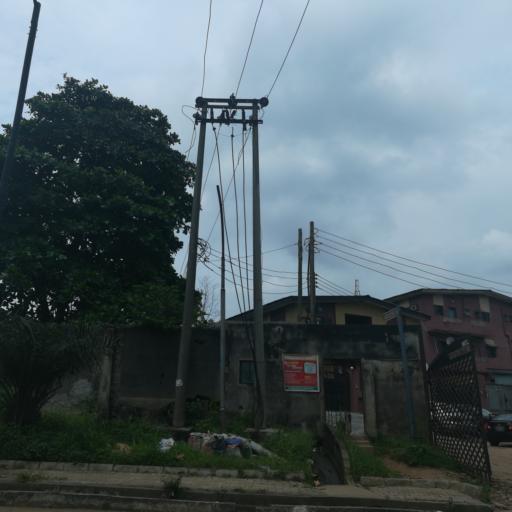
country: NG
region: Lagos
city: Ojota
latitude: 6.5751
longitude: 3.3968
